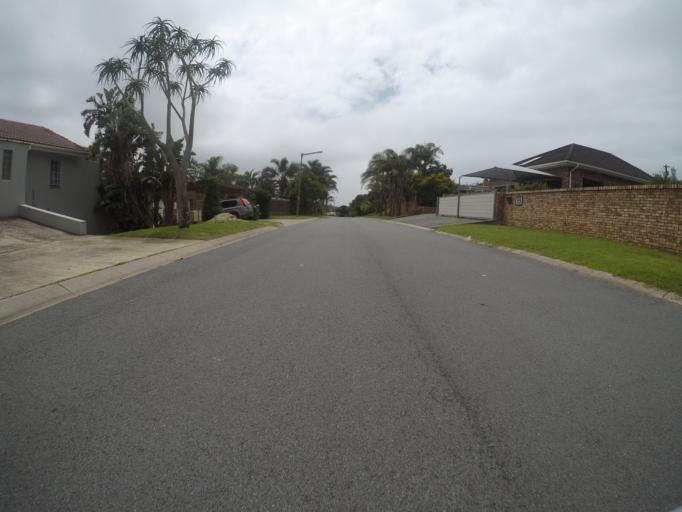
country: ZA
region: Eastern Cape
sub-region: Buffalo City Metropolitan Municipality
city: East London
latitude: -32.9921
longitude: 27.9364
